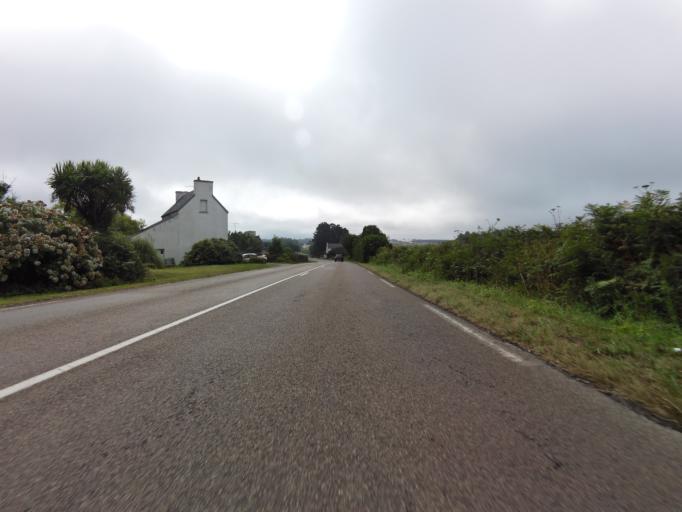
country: FR
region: Brittany
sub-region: Departement du Finistere
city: Plouhinec
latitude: 48.0109
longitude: -4.4640
